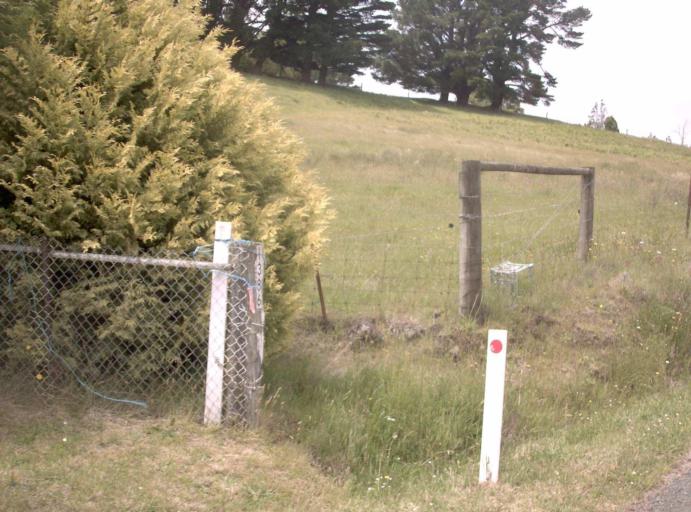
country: AU
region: Victoria
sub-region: Latrobe
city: Traralgon
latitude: -38.4201
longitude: 146.6093
